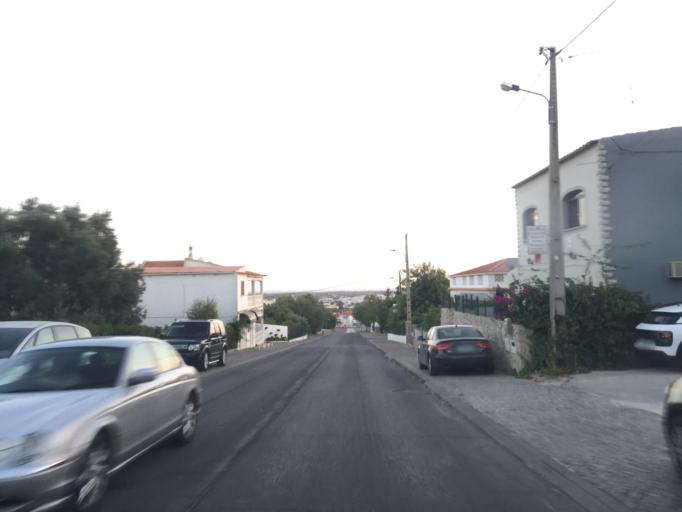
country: PT
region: Faro
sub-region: Loule
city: Almancil
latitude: 37.0996
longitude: -8.0231
